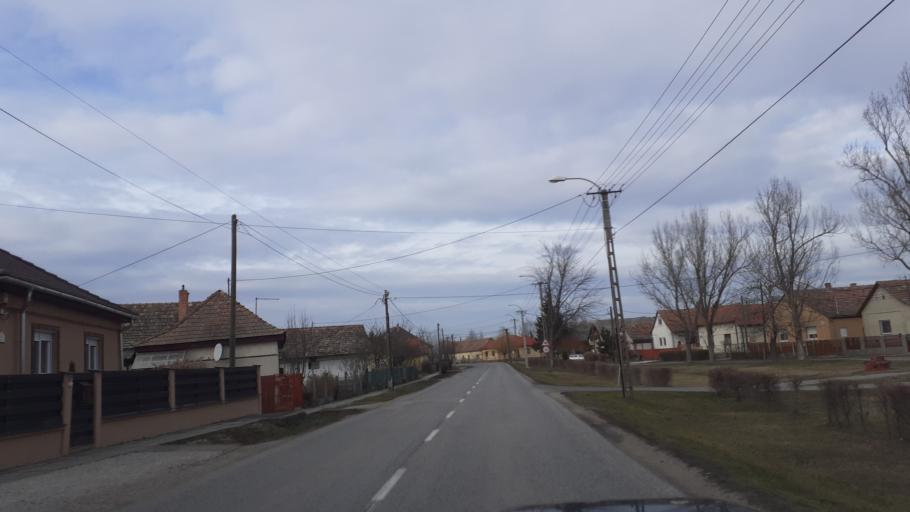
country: HU
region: Fejer
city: Szabadbattyan
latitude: 47.0780
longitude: 18.4128
